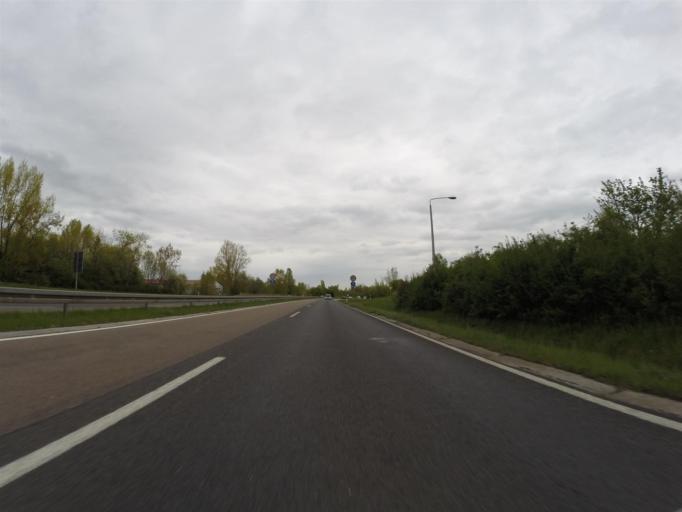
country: DE
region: Saxony-Anhalt
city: Schkopau
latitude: 51.4030
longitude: 11.9748
